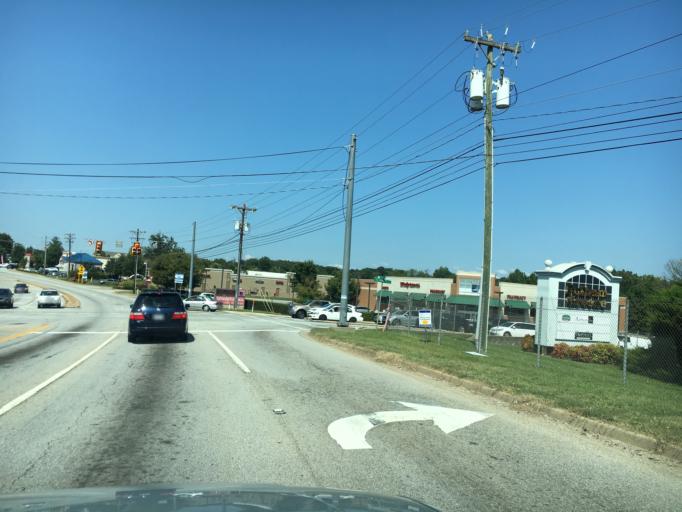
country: US
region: South Carolina
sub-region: Greenville County
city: Five Forks
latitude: 34.8597
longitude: -82.2614
